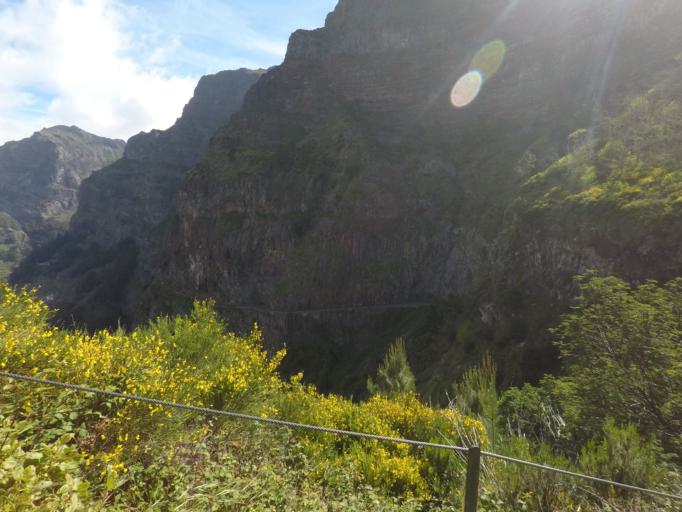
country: PT
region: Madeira
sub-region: Camara de Lobos
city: Curral das Freiras
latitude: 32.7112
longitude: -16.9645
